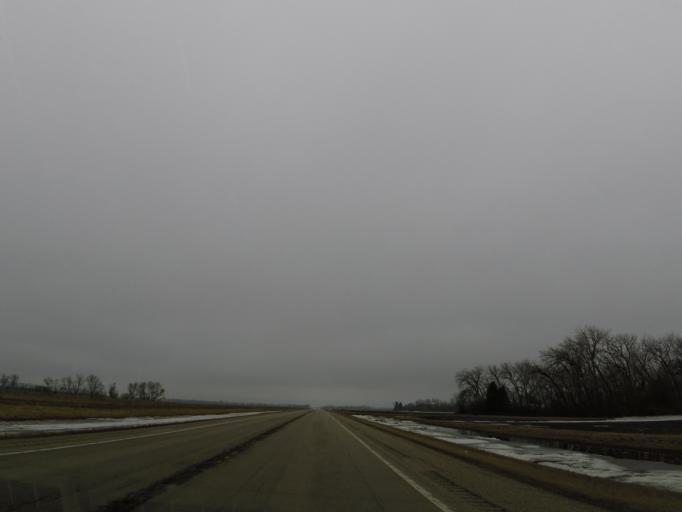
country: US
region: North Dakota
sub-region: Walsh County
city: Grafton
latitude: 48.5673
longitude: -97.4480
